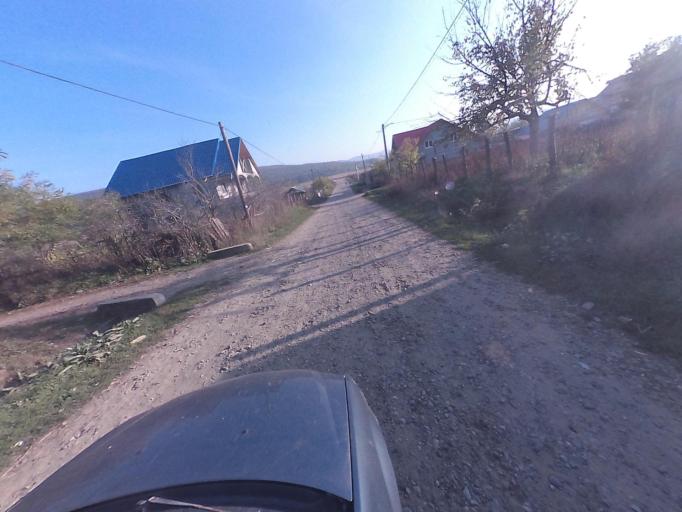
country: RO
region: Vaslui
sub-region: Comuna Bacesti
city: Bacesti
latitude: 46.8197
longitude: 27.2384
